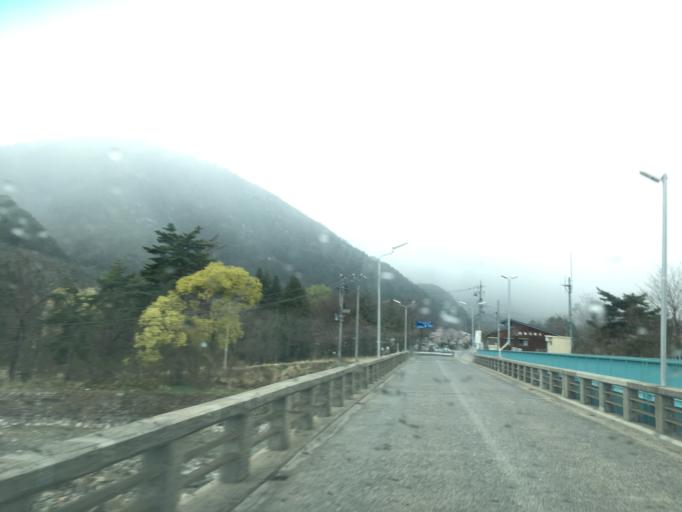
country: JP
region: Nagano
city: Omachi
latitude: 36.5130
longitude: 137.8190
